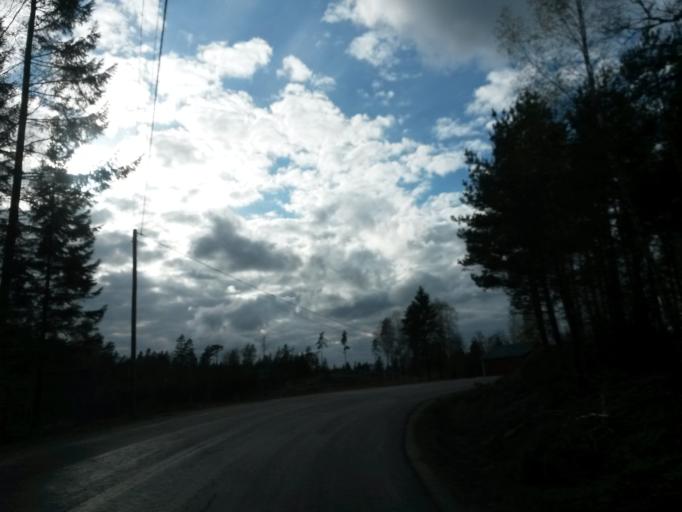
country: SE
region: Vaestra Goetaland
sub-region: Vargarda Kommun
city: Jonstorp
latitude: 58.0090
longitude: 12.6724
